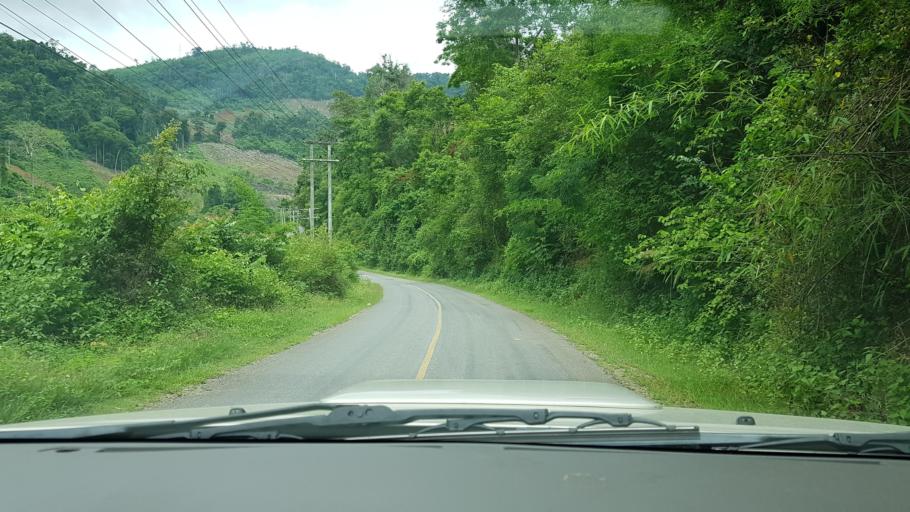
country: TH
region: Nan
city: Chaloem Phra Kiat
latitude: 19.9479
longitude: 101.2472
